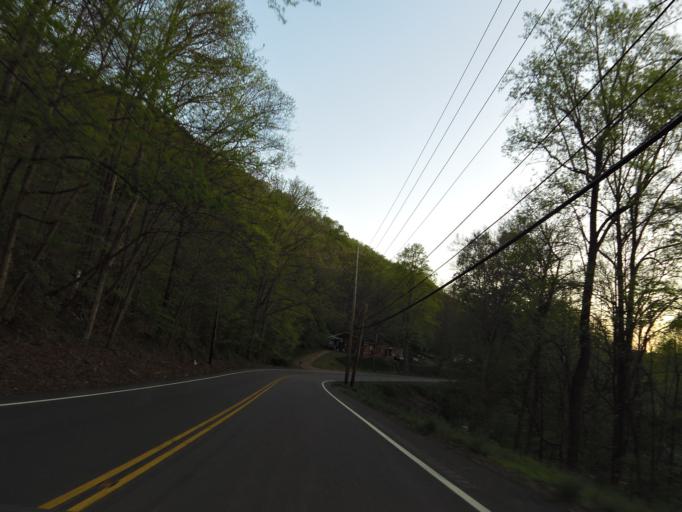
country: US
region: Tennessee
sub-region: Campbell County
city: LaFollette
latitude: 36.4071
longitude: -84.1116
